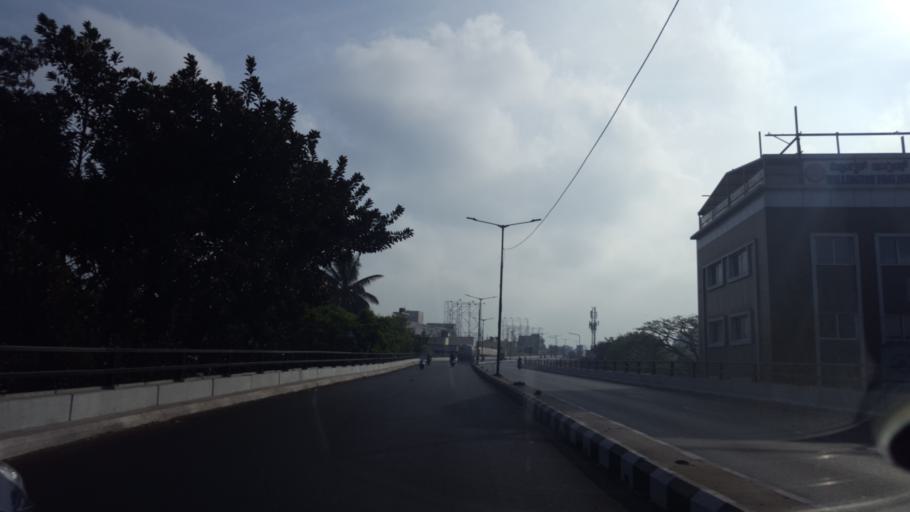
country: IN
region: Karnataka
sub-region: Bangalore Urban
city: Bangalore
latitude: 12.9637
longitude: 77.5689
